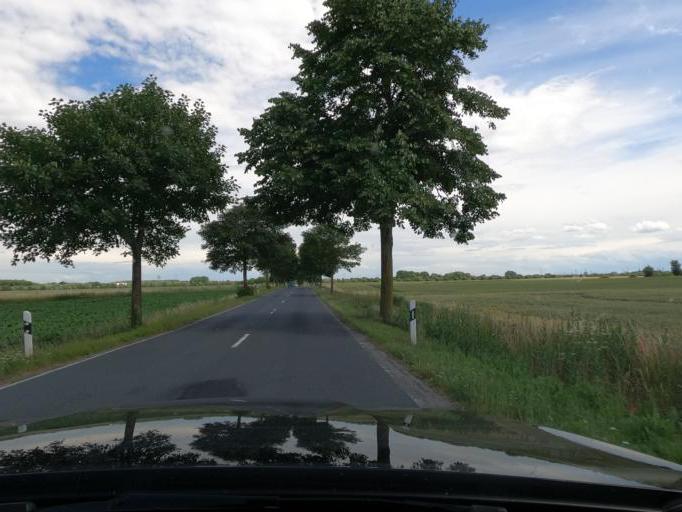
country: DE
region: Lower Saxony
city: Lengede
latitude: 52.1889
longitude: 10.3031
